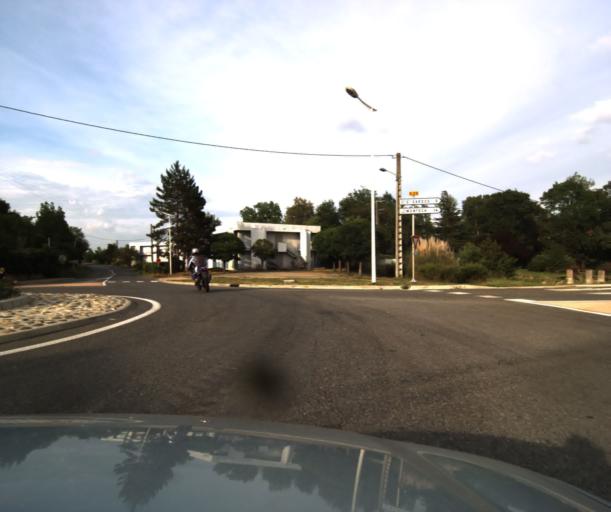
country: FR
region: Midi-Pyrenees
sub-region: Departement du Tarn-et-Garonne
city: Castelsarrasin
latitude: 43.9316
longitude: 1.0853
